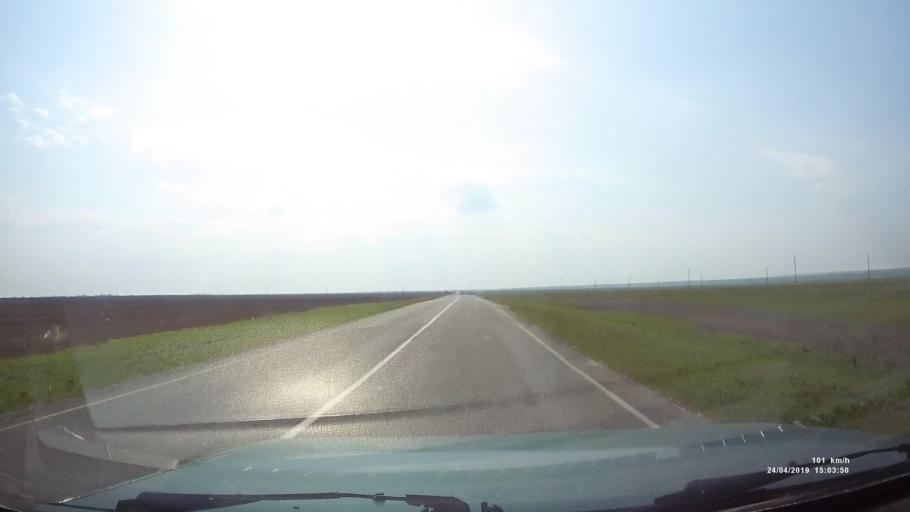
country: RU
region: Rostov
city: Remontnoye
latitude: 46.5640
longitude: 43.4834
